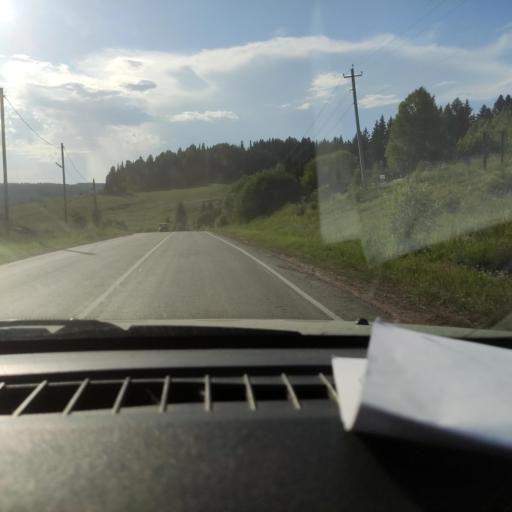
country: RU
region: Perm
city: Krasnokamsk
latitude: 58.1455
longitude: 55.7270
